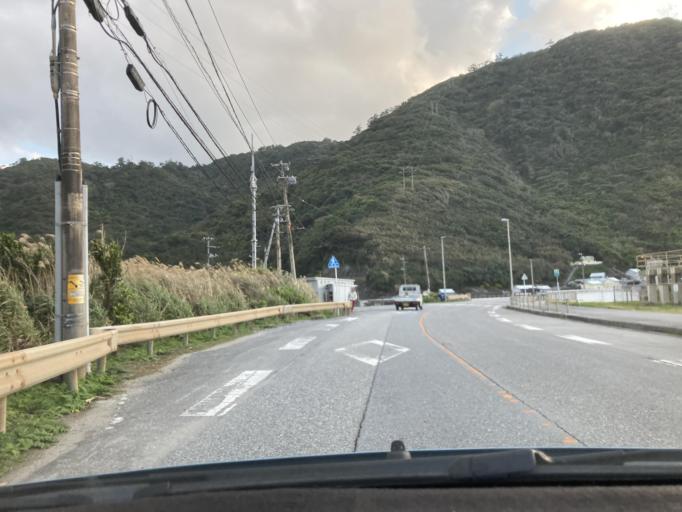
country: JP
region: Okinawa
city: Nago
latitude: 26.7984
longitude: 128.2326
